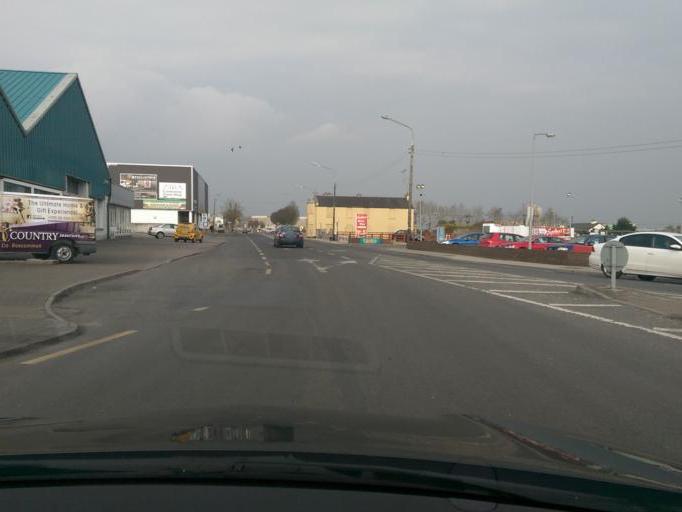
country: IE
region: Connaught
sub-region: Roscommon
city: Roscommon
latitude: 53.6291
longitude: -8.1871
